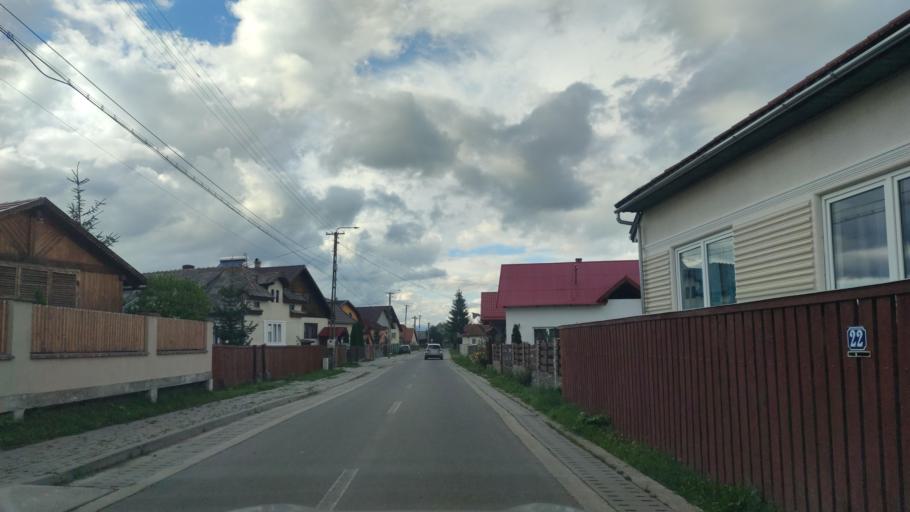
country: RO
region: Harghita
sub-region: Comuna Remetea
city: Remetea
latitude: 46.8029
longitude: 25.4501
